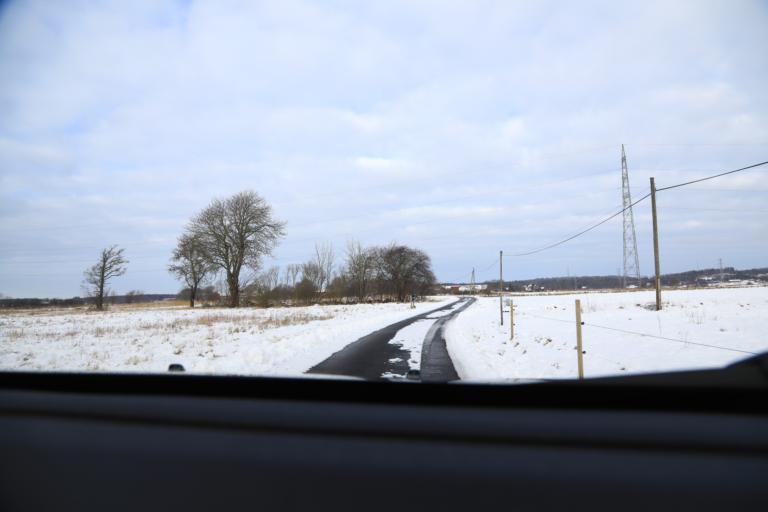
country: SE
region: Halland
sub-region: Kungsbacka Kommun
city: Frillesas
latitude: 57.2270
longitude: 12.1886
